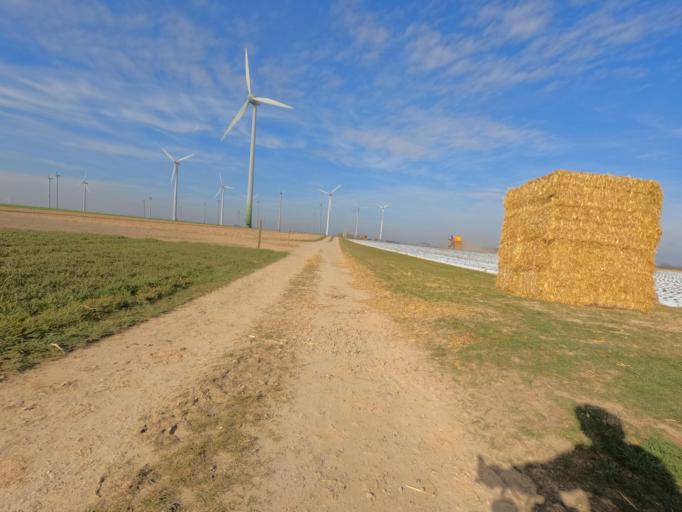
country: DE
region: North Rhine-Westphalia
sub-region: Regierungsbezirk Koln
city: Linnich
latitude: 51.0174
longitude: 6.3172
